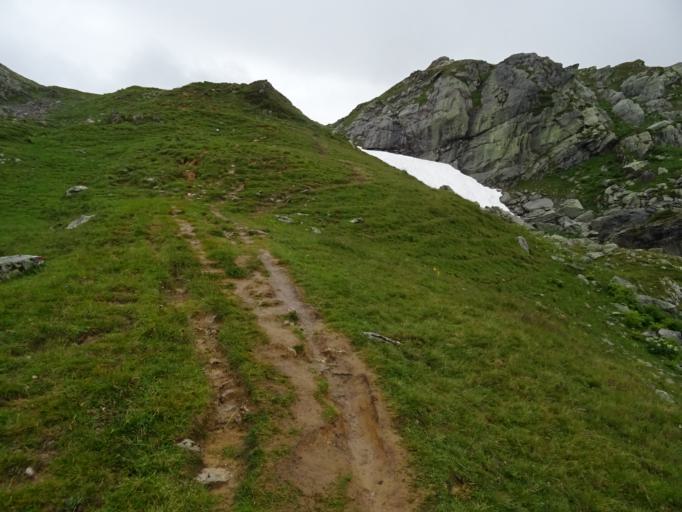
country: AT
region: Salzburg
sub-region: Politischer Bezirk Tamsweg
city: Tweng
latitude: 47.2721
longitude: 13.5855
